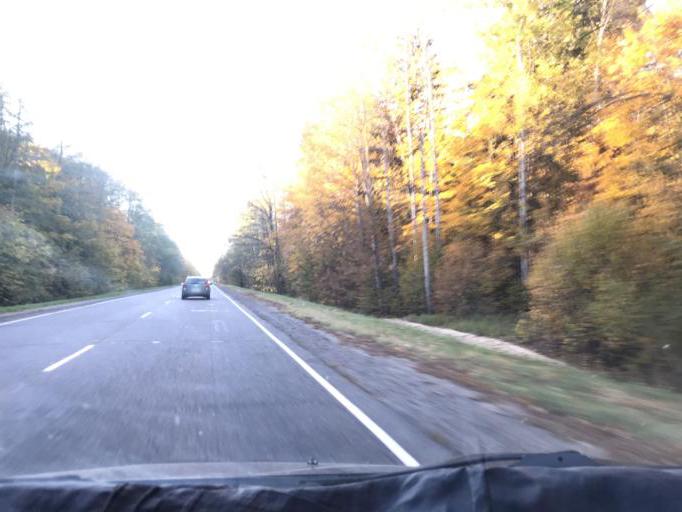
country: BY
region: Gomel
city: Pyetrykaw
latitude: 52.2663
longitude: 28.2992
